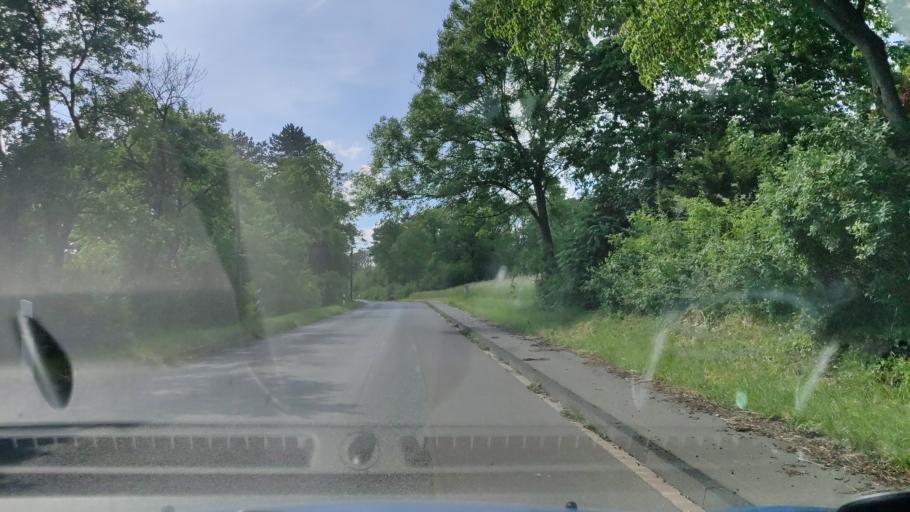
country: DE
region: Lower Saxony
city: Rosdorf
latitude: 51.5351
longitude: 9.8477
